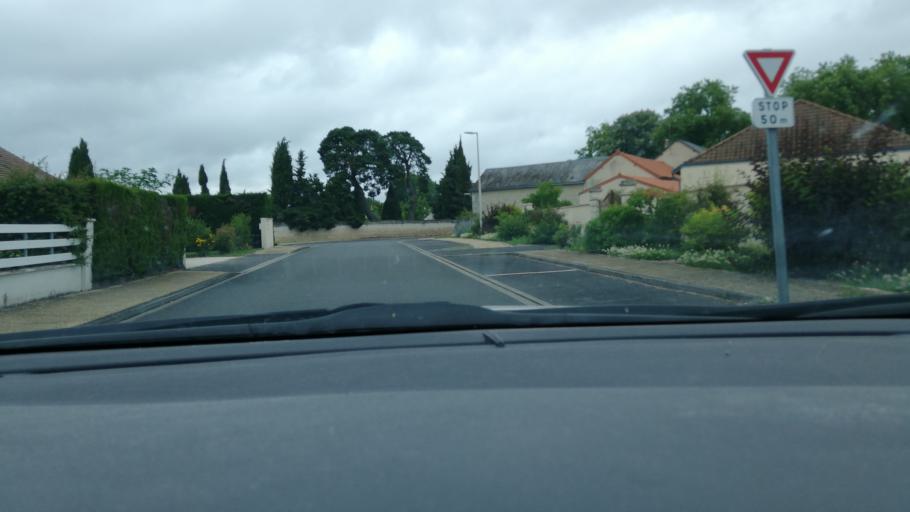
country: FR
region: Poitou-Charentes
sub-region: Departement de la Vienne
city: Antran
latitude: 46.8750
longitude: 0.5671
